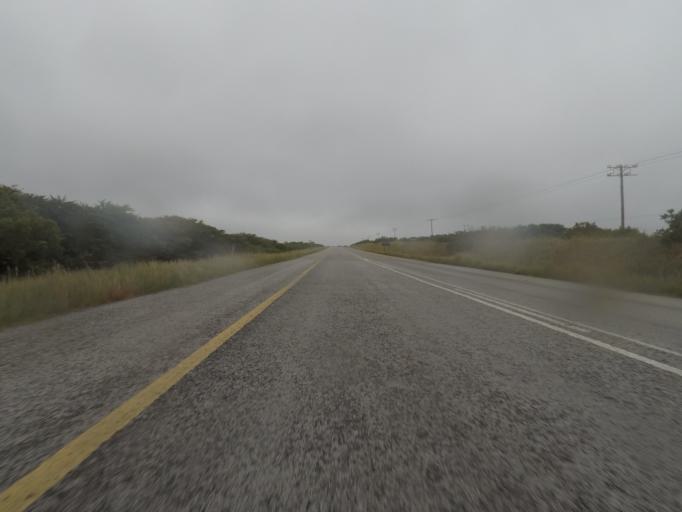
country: ZA
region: Eastern Cape
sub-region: Cacadu District Municipality
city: Grahamstown
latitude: -33.6434
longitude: 26.3599
